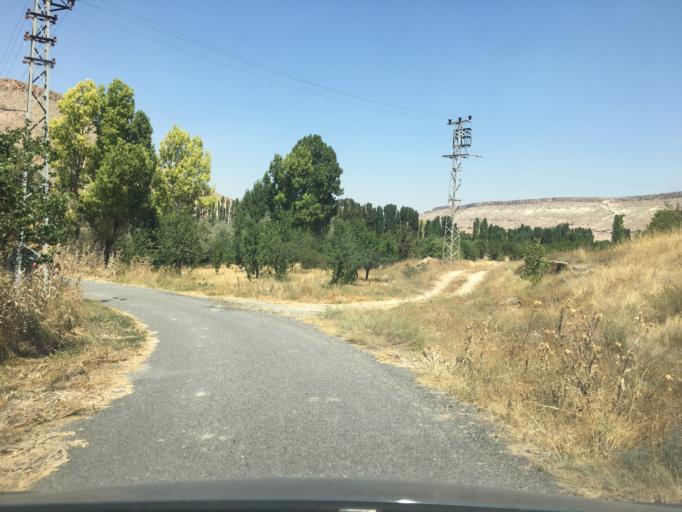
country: TR
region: Kayseri
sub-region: Yesilhisar
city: Yesilhisar
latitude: 38.4672
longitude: 34.9642
